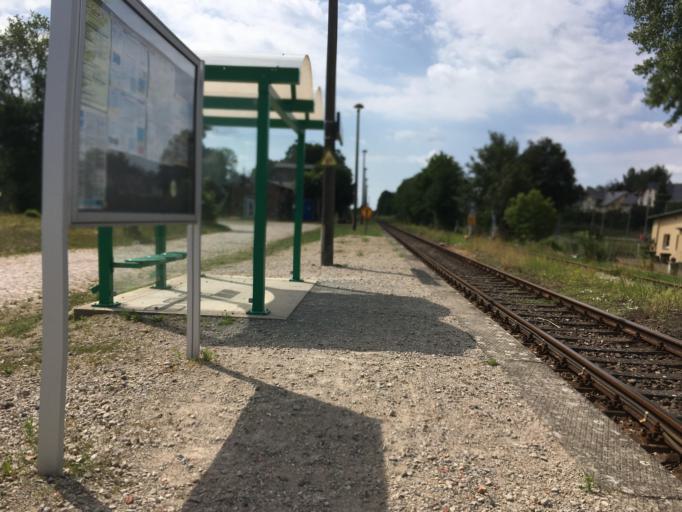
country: DE
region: Brandenburg
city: Friedrichswalde
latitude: 53.0306
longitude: 13.7031
